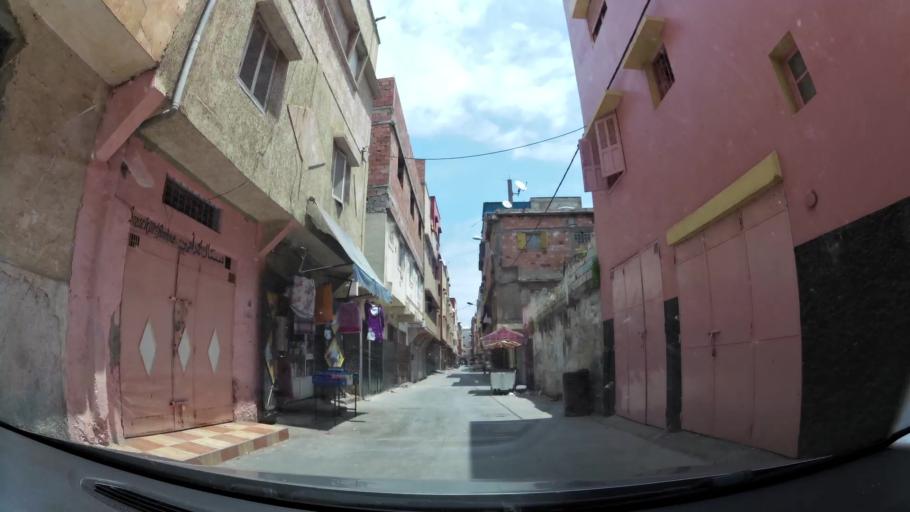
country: MA
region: Rabat-Sale-Zemmour-Zaer
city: Sale
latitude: 34.0517
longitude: -6.7904
